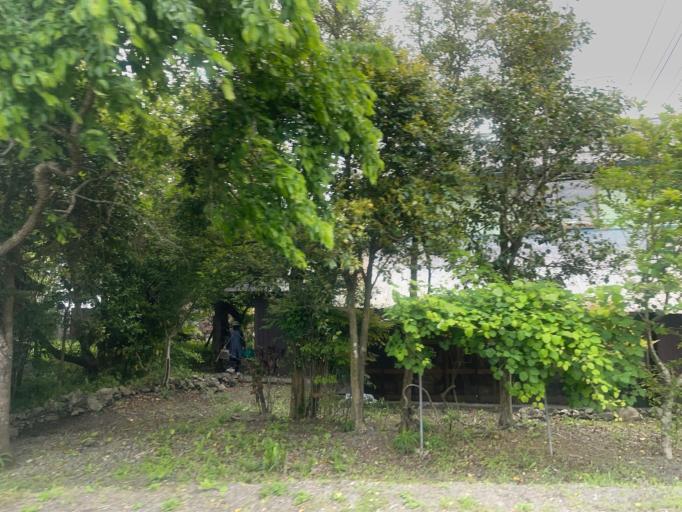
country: JP
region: Tochigi
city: Tanuma
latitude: 36.4712
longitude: 139.6286
